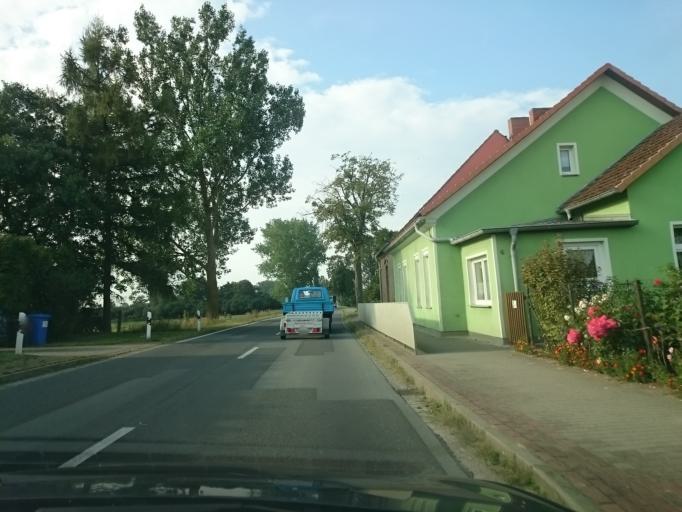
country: DE
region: Mecklenburg-Vorpommern
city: Borrentin
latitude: 53.8475
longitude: 12.9985
